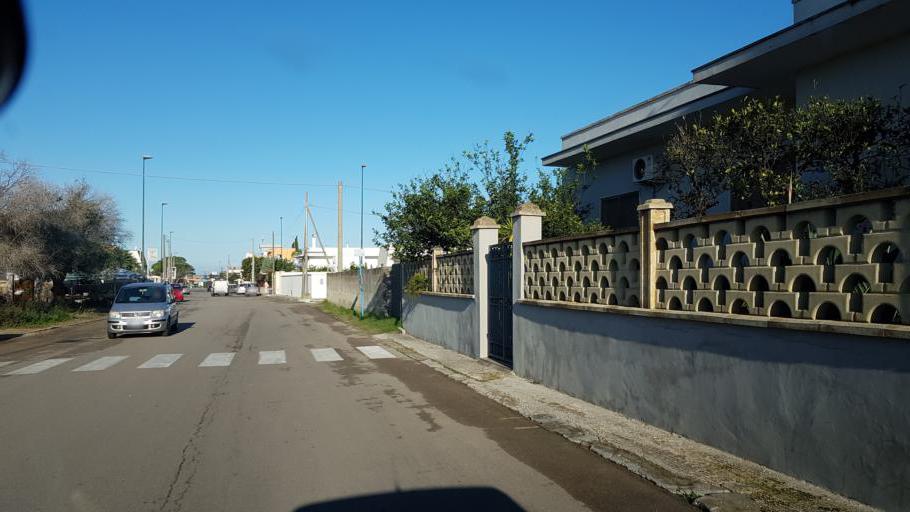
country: IT
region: Apulia
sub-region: Provincia di Brindisi
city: Torchiarolo
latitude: 40.4841
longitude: 18.0484
